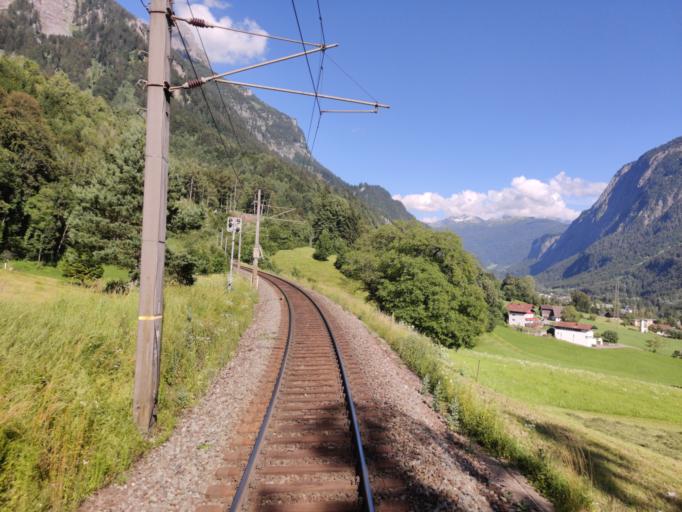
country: AT
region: Vorarlberg
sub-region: Politischer Bezirk Bludenz
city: Innerbraz
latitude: 47.1488
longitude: 9.9125
